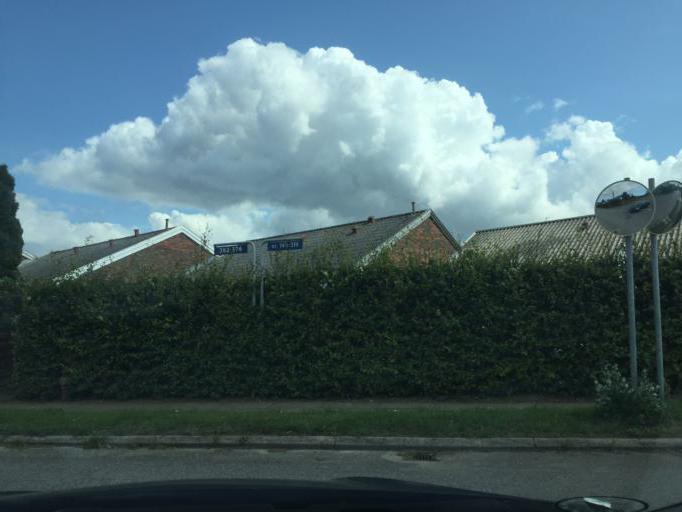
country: DK
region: South Denmark
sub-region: Odense Kommune
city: Neder Holluf
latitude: 55.3610
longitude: 10.4536
